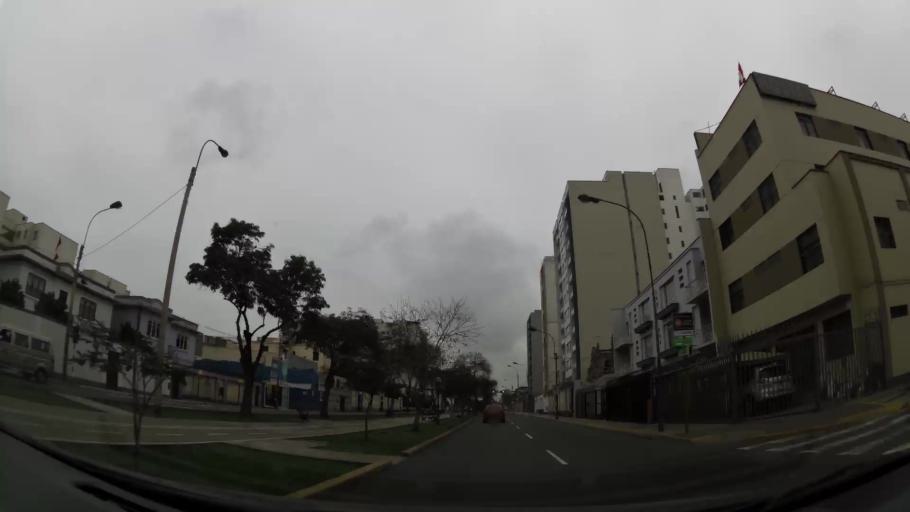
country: PE
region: Lima
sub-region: Lima
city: San Isidro
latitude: -12.1087
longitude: -77.0306
